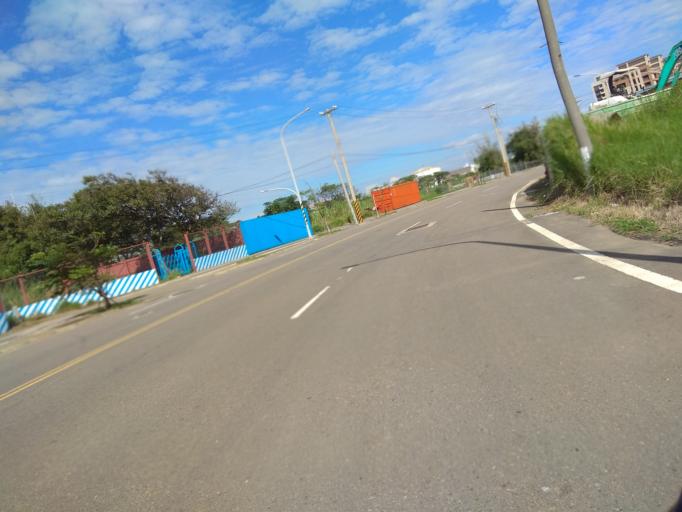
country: TW
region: Taiwan
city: Taoyuan City
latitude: 25.0433
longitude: 121.1336
